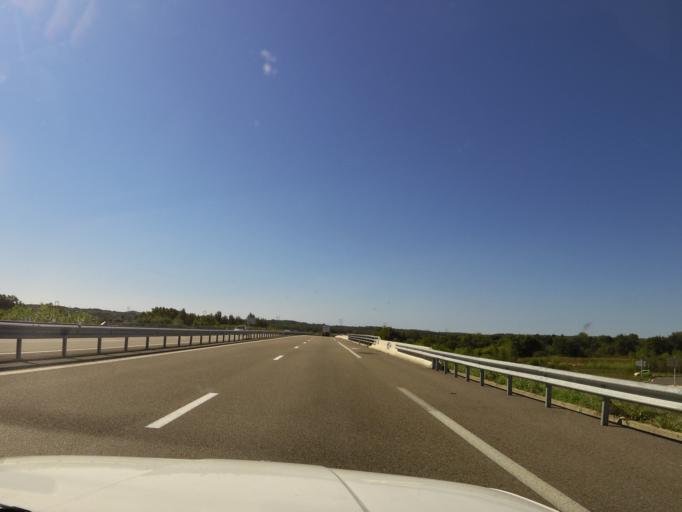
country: FR
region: Languedoc-Roussillon
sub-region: Departement du Gard
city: La Calmette
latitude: 43.9336
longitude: 4.2543
